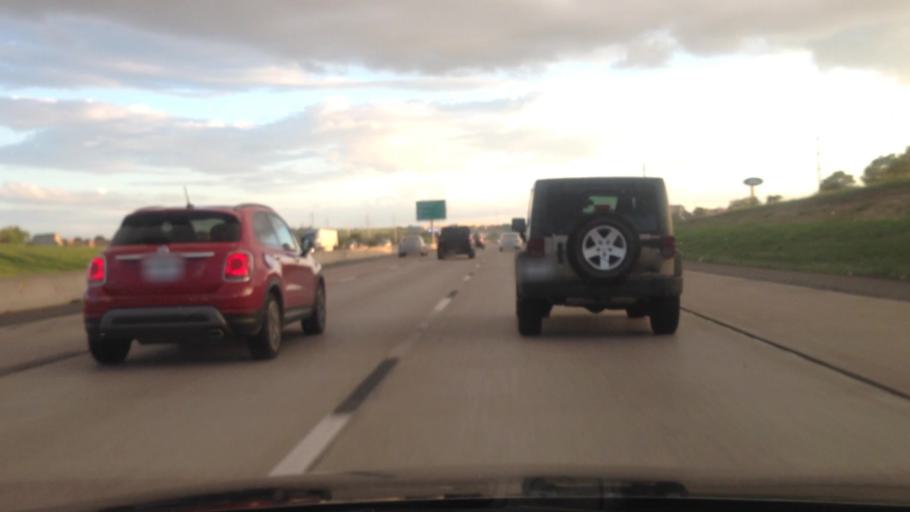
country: US
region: Texas
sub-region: Tarrant County
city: White Settlement
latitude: 32.7600
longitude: -97.4781
